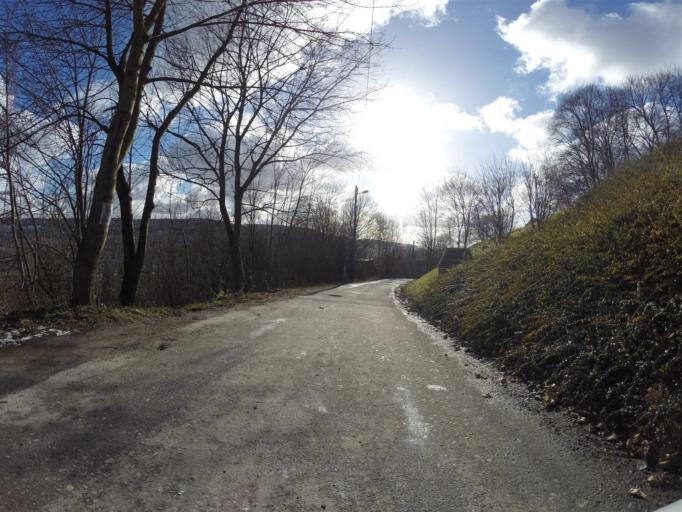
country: DE
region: Thuringia
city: Neuengonna
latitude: 50.9629
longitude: 11.6199
